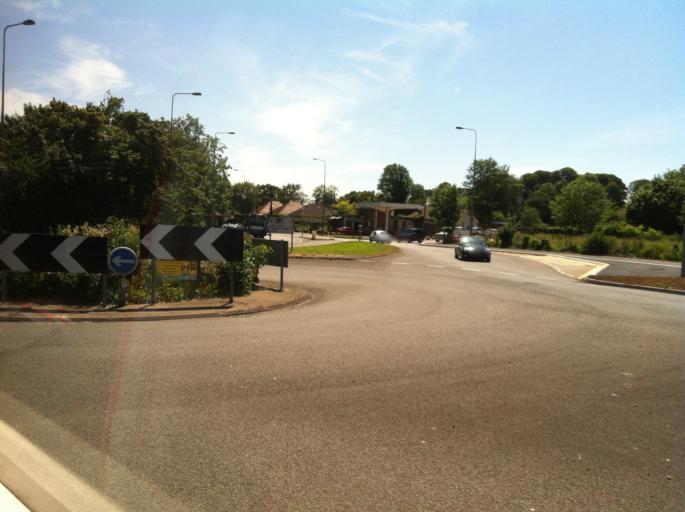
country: GB
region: Wales
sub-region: Vale of Glamorgan
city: Barry
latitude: 51.4426
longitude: -3.2639
